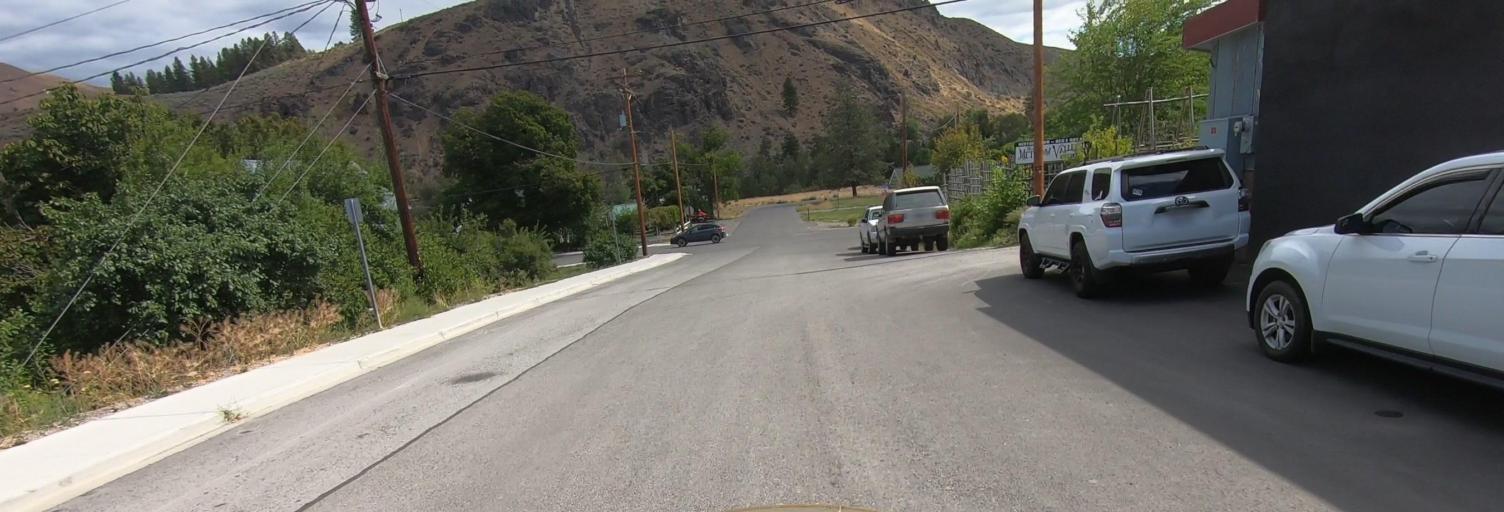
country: US
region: Washington
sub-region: Okanogan County
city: Brewster
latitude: 48.3660
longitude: -120.1211
